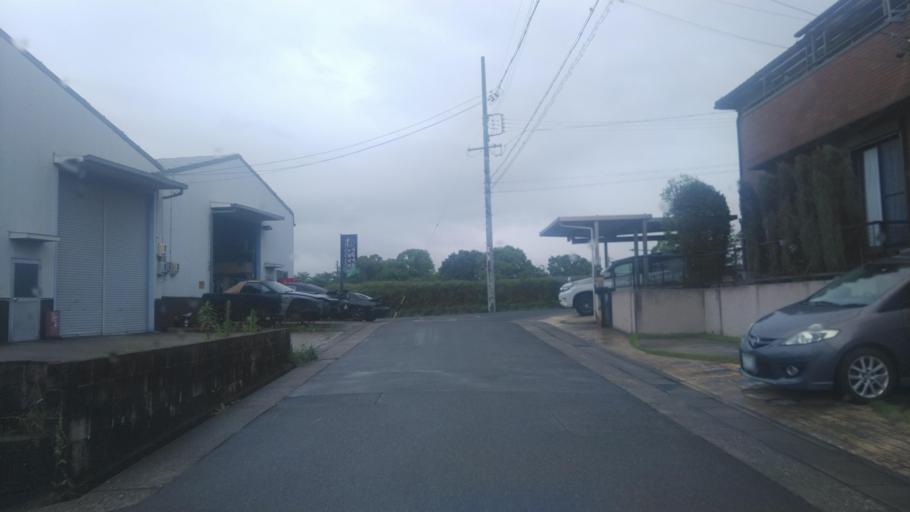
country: JP
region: Aichi
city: Kasugai
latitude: 35.2539
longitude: 137.0178
